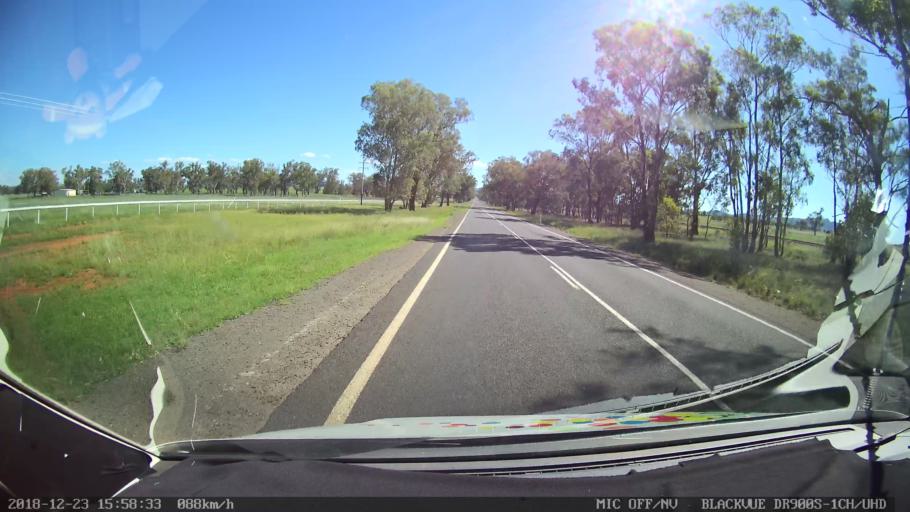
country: AU
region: New South Wales
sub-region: Tamworth Municipality
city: Phillip
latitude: -31.1896
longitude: 150.8407
